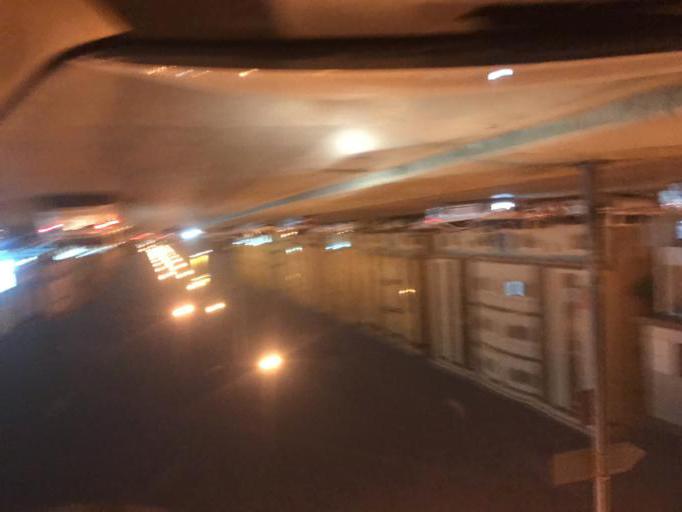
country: SA
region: Ar Riyad
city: Riyadh
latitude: 24.8194
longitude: 46.7953
